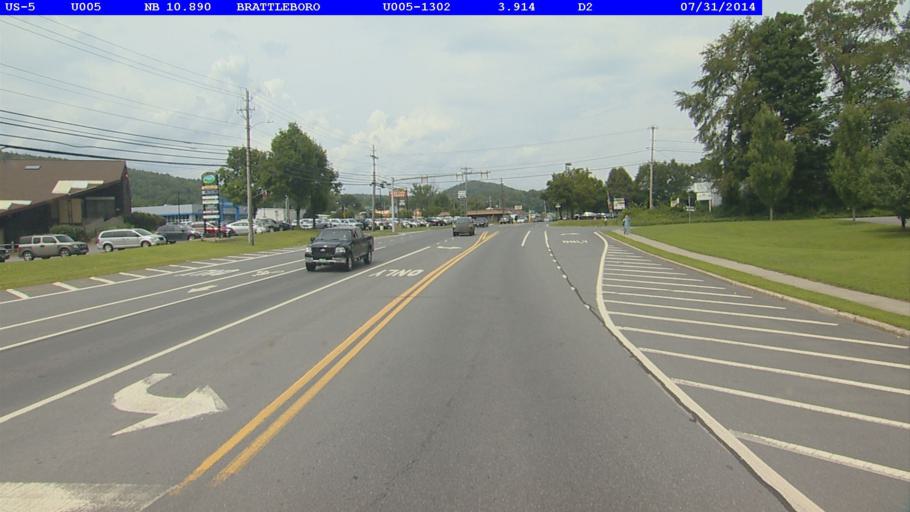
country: US
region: Vermont
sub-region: Windham County
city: Brattleboro
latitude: 42.8752
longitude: -72.5602
